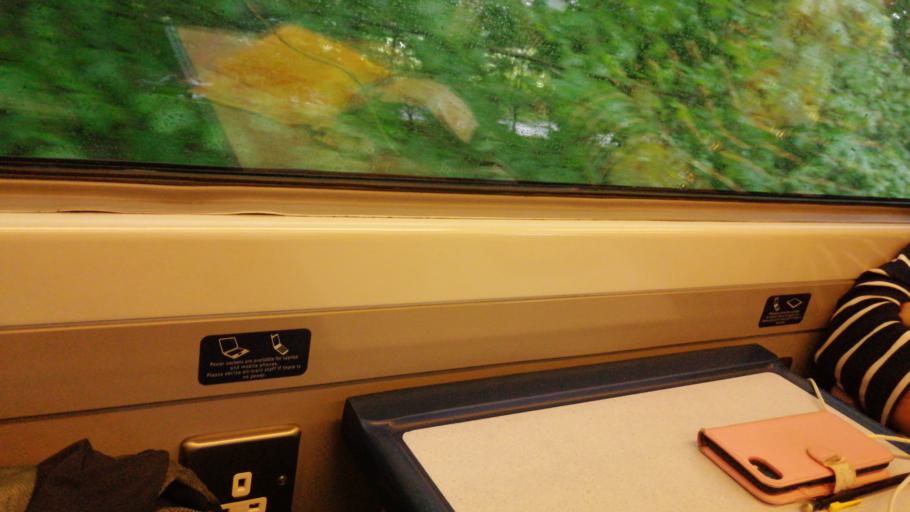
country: GB
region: Scotland
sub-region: Highland
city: Golspie
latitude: 57.9855
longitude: -3.9486
